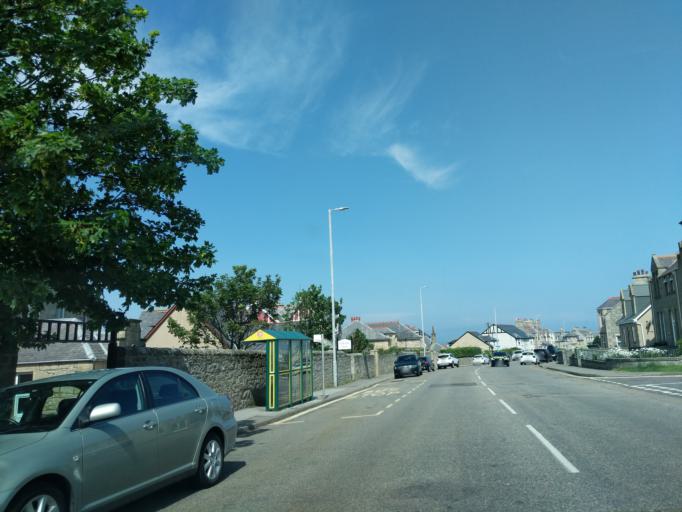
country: GB
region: Scotland
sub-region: Moray
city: Lossiemouth
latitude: 57.7219
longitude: -3.2941
